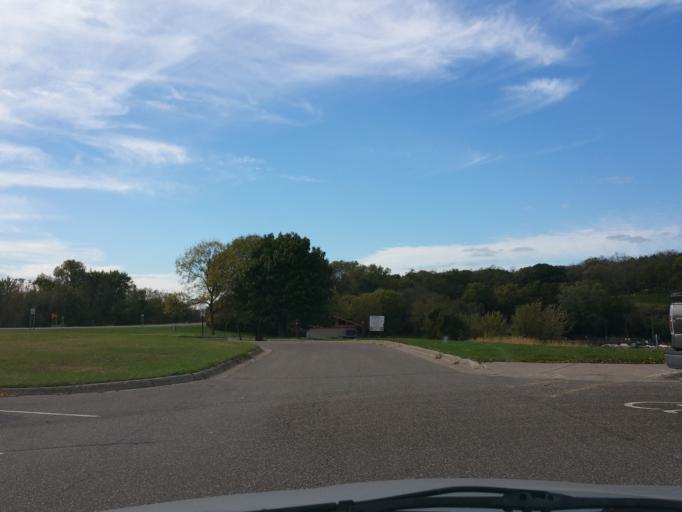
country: US
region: Wisconsin
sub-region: Pierce County
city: Prescott
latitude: 44.7496
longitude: -92.8110
